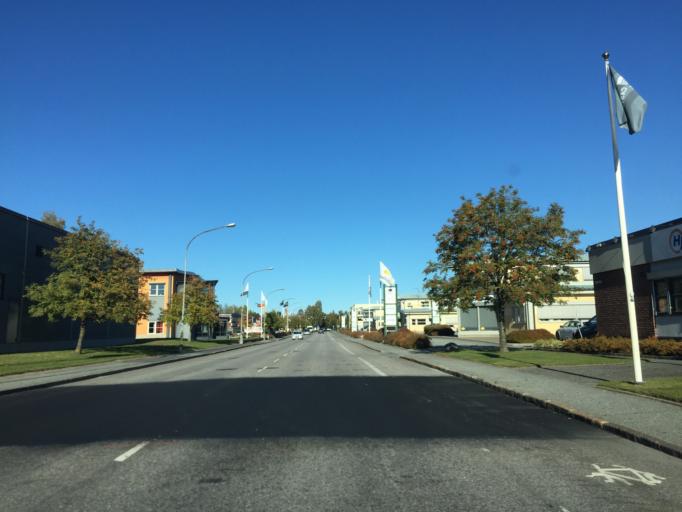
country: SE
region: OErebro
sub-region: Orebro Kommun
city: Orebro
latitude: 59.2599
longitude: 15.1799
